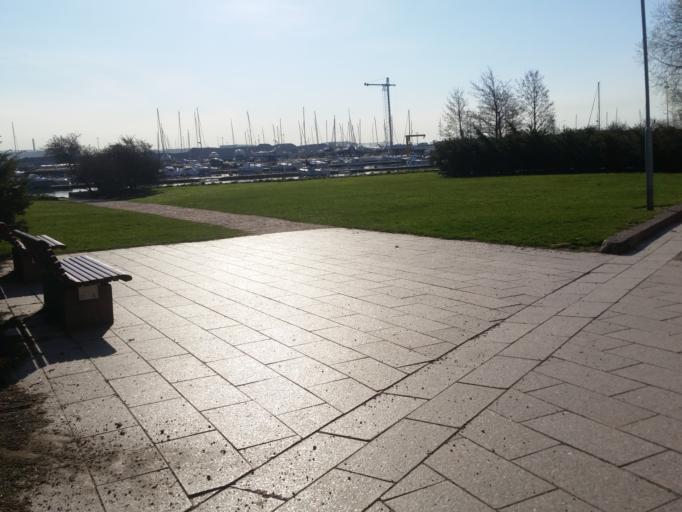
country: FI
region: Uusimaa
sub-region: Helsinki
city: Helsinki
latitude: 60.1537
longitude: 24.8881
